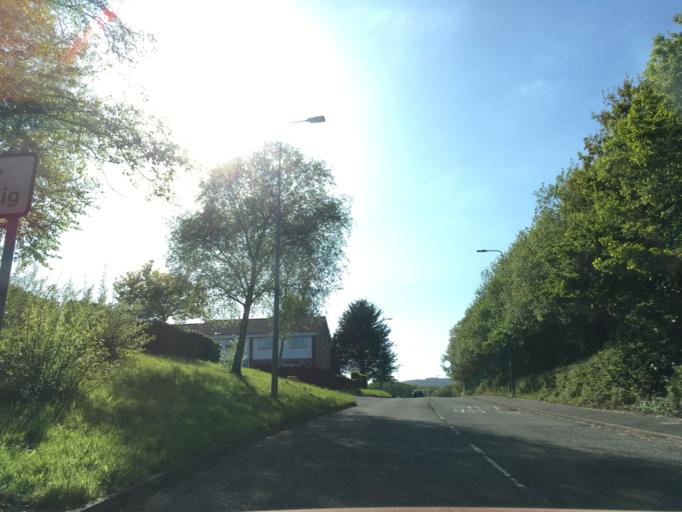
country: GB
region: Wales
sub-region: Cardiff
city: Cardiff
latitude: 51.5303
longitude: -3.1527
